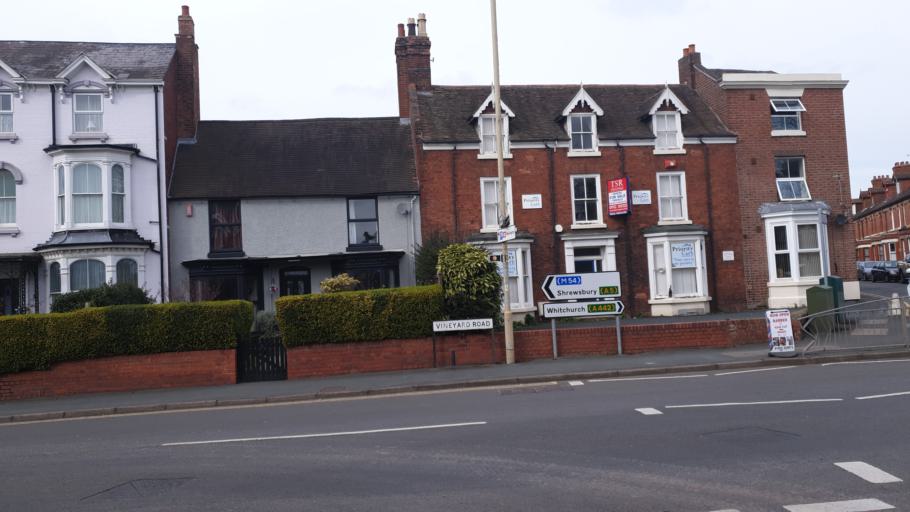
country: GB
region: England
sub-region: Telford and Wrekin
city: Wellington
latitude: 52.7032
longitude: -2.5186
